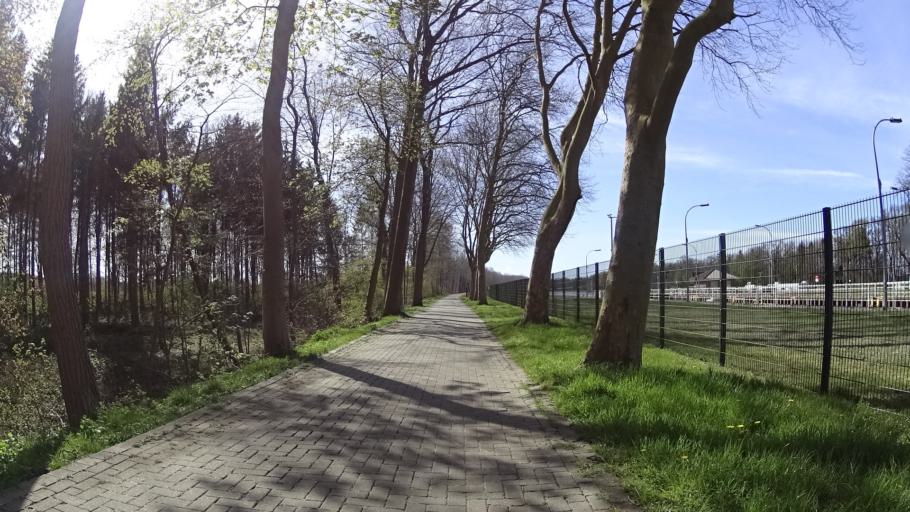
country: DE
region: Lower Saxony
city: Geeste
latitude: 52.6217
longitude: 7.3084
